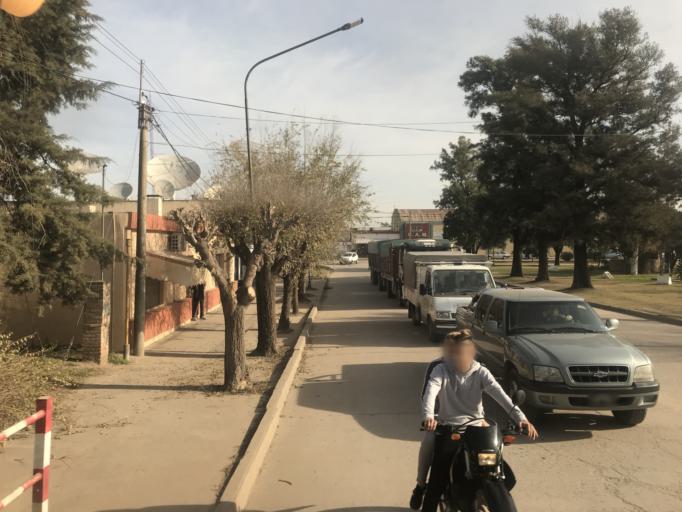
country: AR
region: Cordoba
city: Laguna Larga
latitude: -31.7798
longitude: -63.8007
